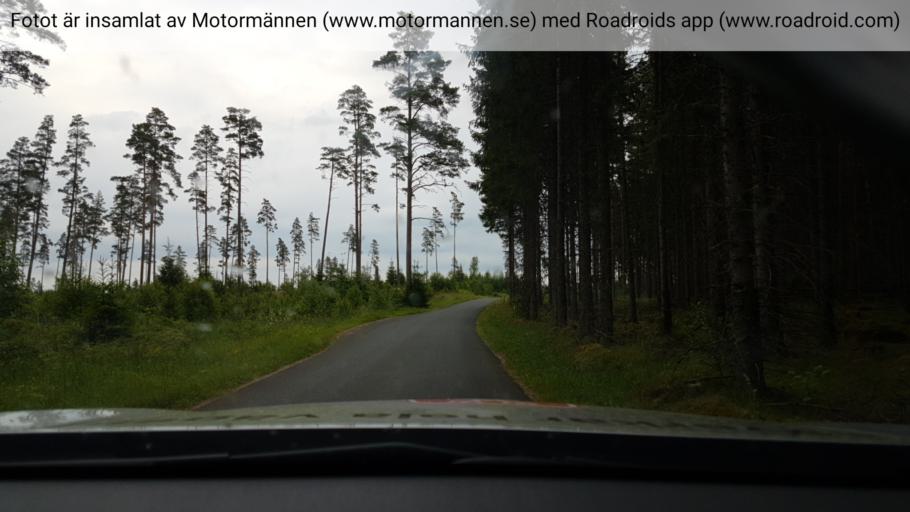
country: SE
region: Joenkoeping
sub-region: Mullsjo Kommun
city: Mullsjoe
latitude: 57.9589
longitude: 13.7207
